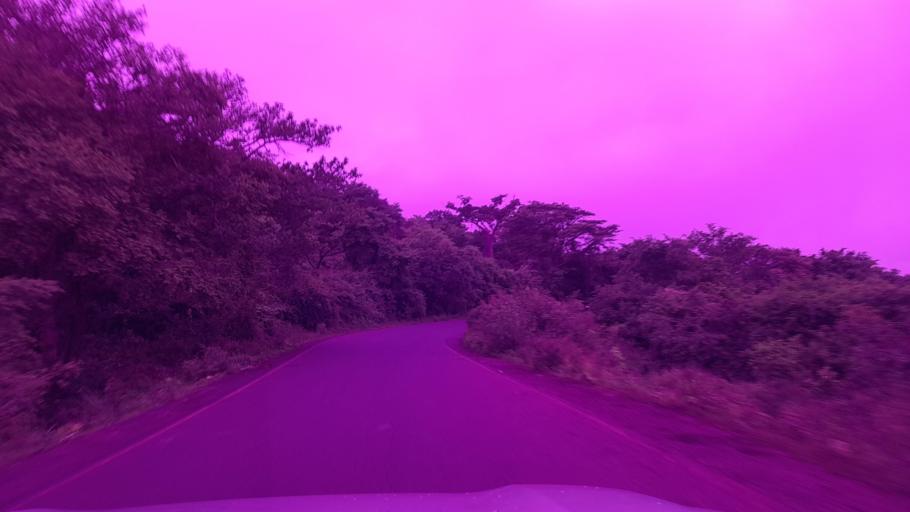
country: ET
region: Oromiya
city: Waliso
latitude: 8.1737
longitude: 37.5834
